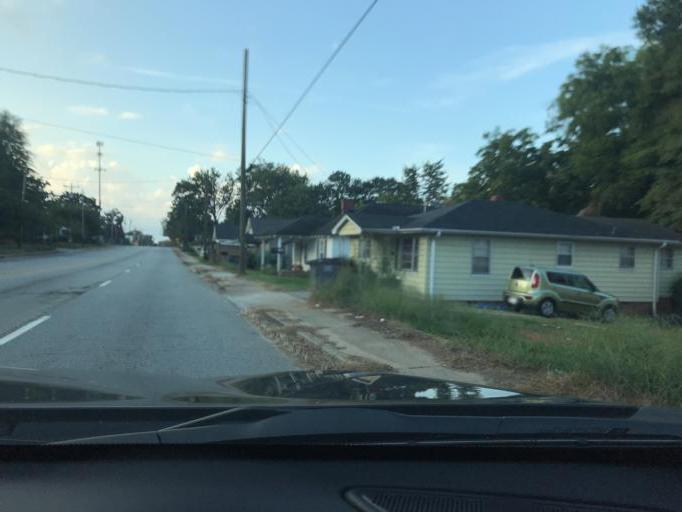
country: US
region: South Carolina
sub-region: Greenville County
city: Welcome
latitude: 34.8384
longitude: -82.4426
